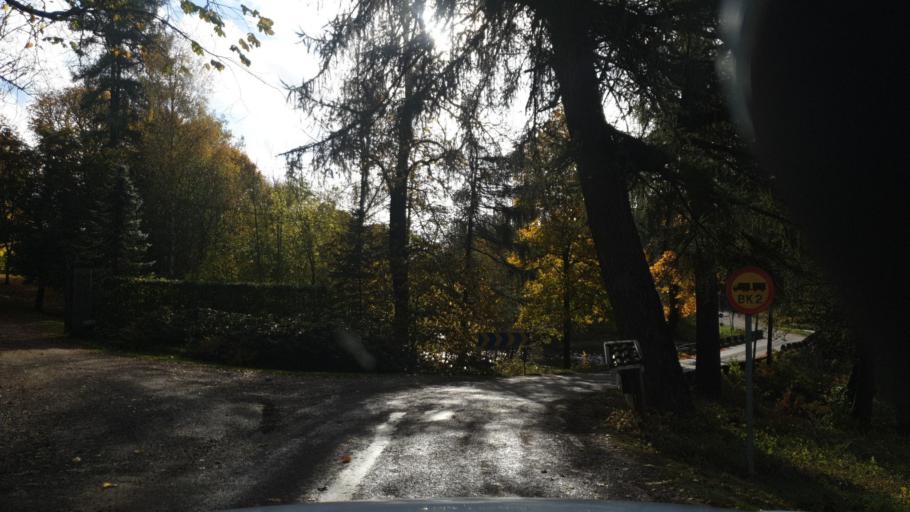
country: SE
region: Vaermland
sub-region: Sunne Kommun
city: Sunne
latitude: 59.6188
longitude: 12.9618
